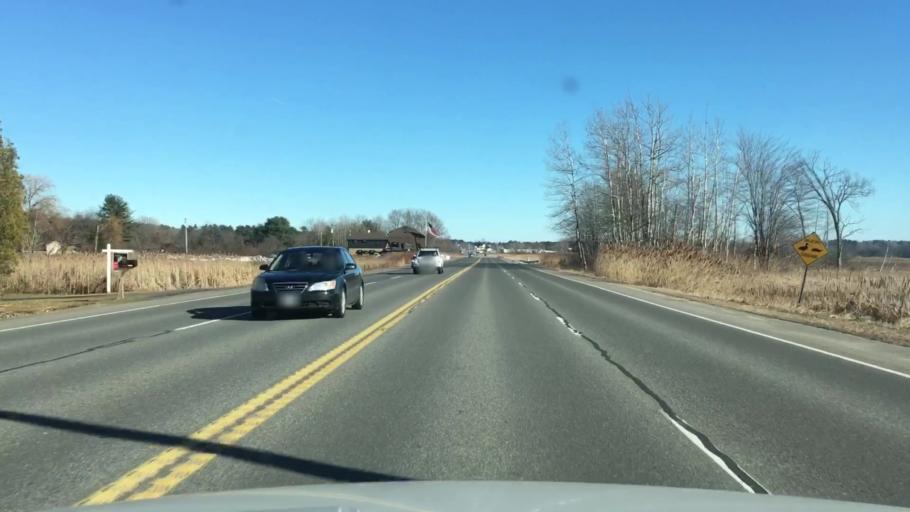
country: US
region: Maine
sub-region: Cumberland County
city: West Scarborough
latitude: 43.5755
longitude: -70.3796
